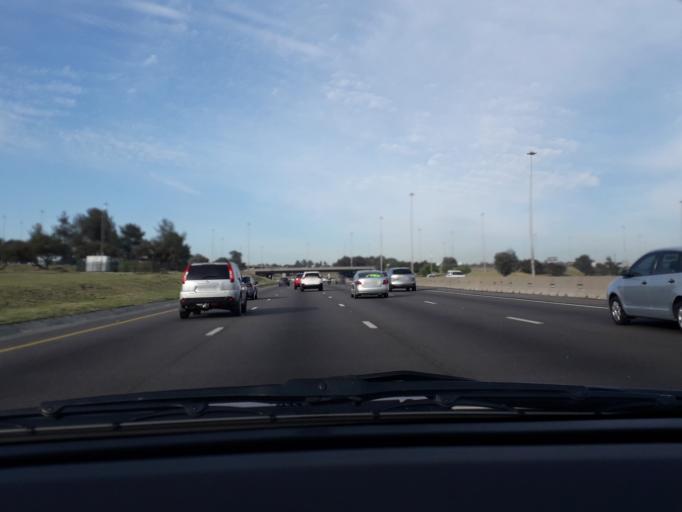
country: ZA
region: Gauteng
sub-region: City of Johannesburg Metropolitan Municipality
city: Midrand
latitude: -26.0443
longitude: 28.1000
